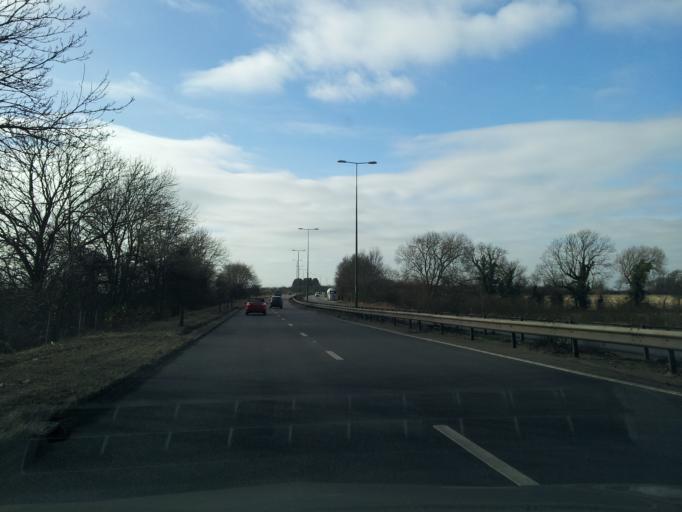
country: GB
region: England
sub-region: Derbyshire
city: Long Eaton
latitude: 52.9125
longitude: -1.3243
